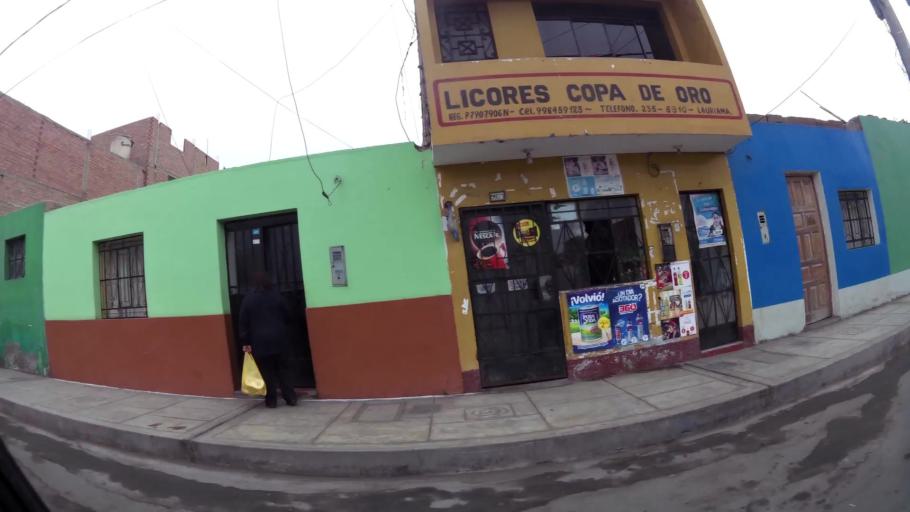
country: PE
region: Lima
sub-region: Barranca
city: Barranca
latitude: -10.7458
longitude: -77.7568
